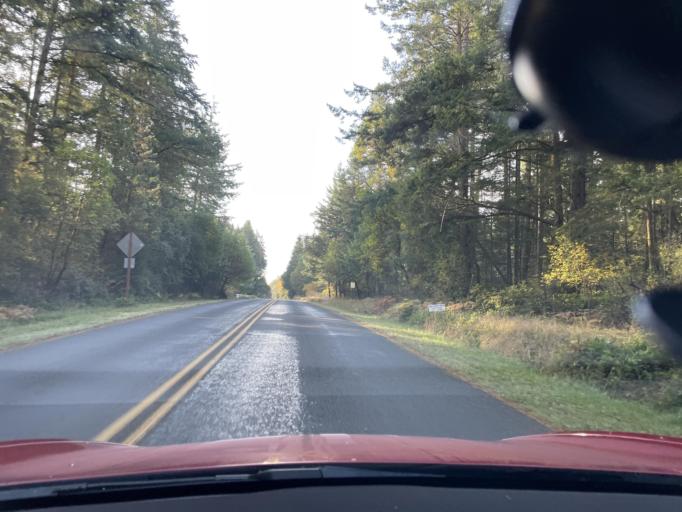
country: US
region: Washington
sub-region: San Juan County
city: Friday Harbor
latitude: 48.5645
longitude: -123.1648
